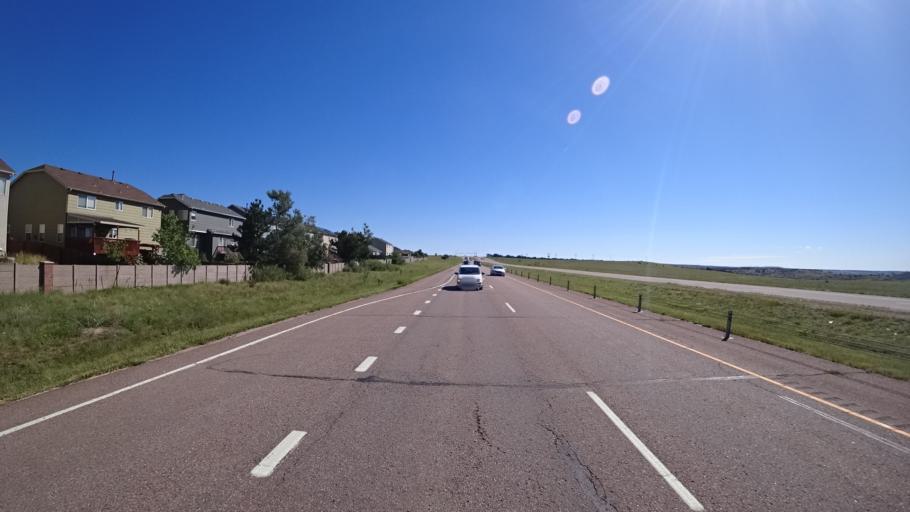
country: US
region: Colorado
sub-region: El Paso County
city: Cimarron Hills
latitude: 38.8600
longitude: -104.6703
